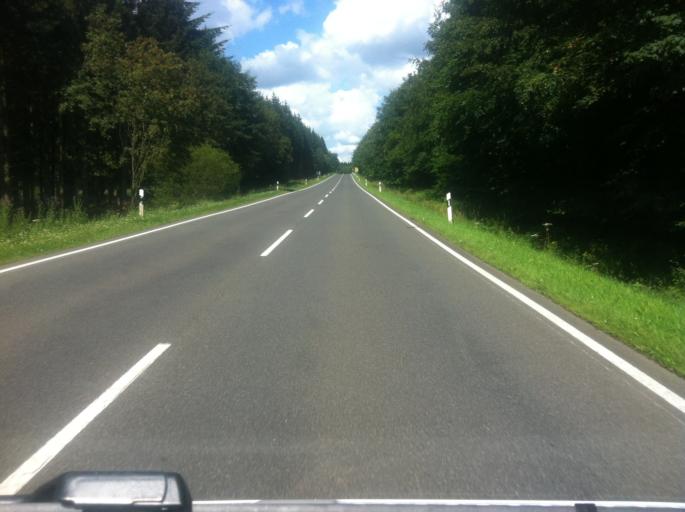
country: DE
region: Rheinland-Pfalz
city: Scheid
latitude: 50.4022
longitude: 6.3664
